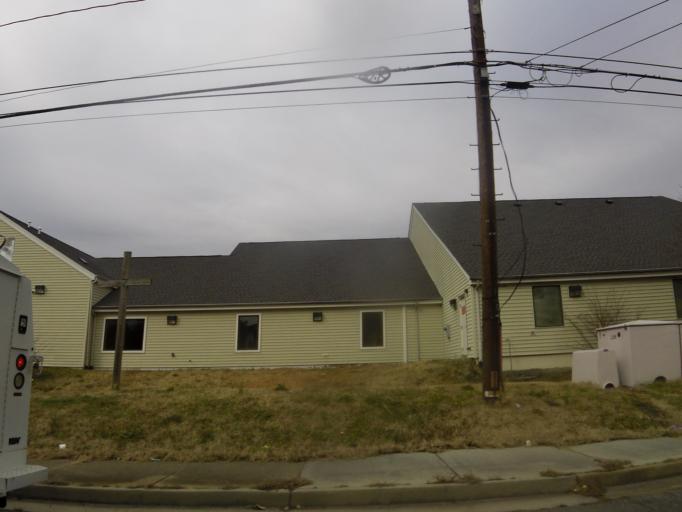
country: US
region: Virginia
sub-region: City of Portsmouth
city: Portsmouth Heights
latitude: 36.8185
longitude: -76.3539
